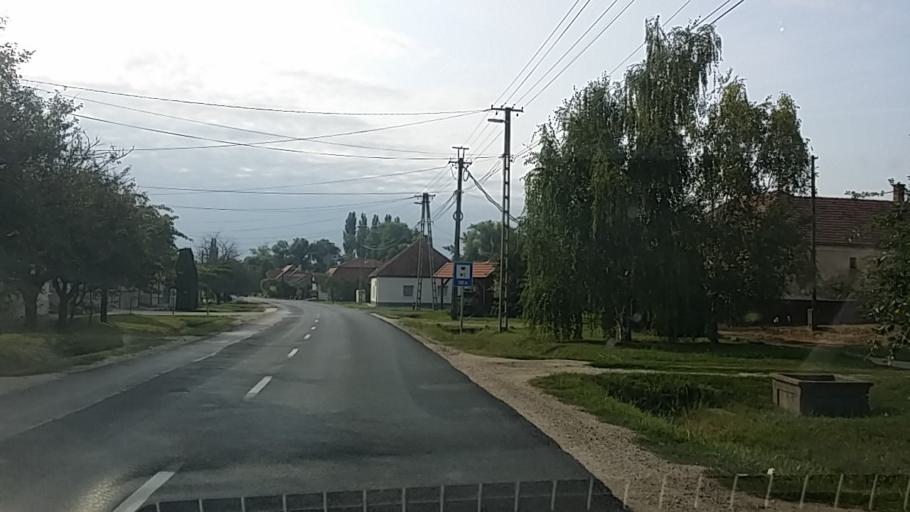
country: HU
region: Gyor-Moson-Sopron
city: Fertoszentmiklos
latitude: 47.6036
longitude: 16.9083
